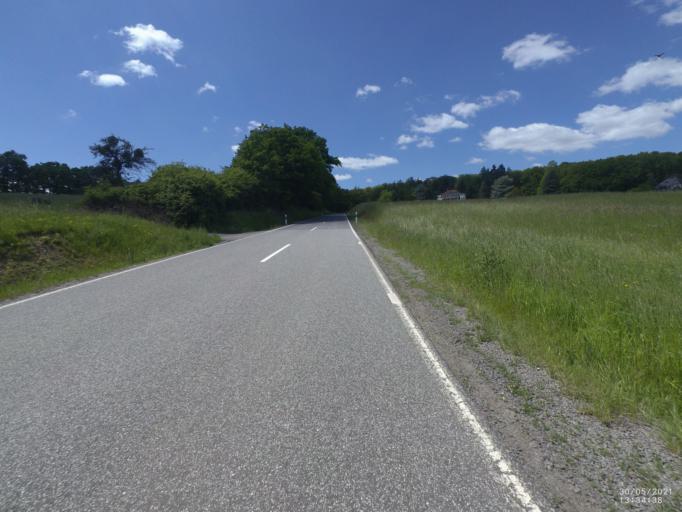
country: DE
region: Rheinland-Pfalz
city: Rhens
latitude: 50.2826
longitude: 7.5894
